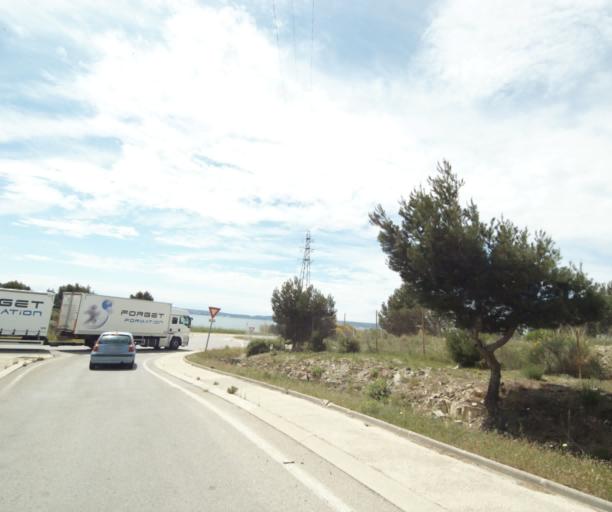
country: FR
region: Provence-Alpes-Cote d'Azur
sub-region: Departement des Bouches-du-Rhone
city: Rognac
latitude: 43.4928
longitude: 5.2045
